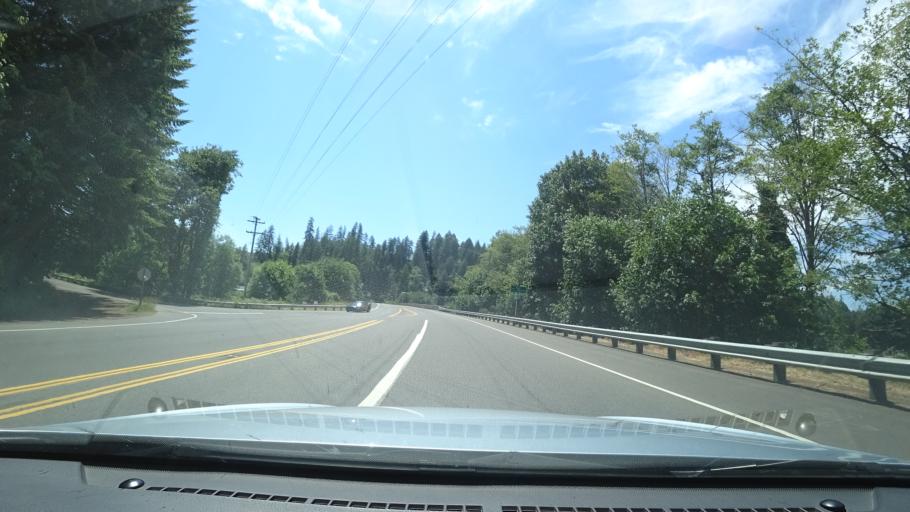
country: US
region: Oregon
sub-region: Lane County
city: Florence
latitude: 44.0330
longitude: -123.8556
